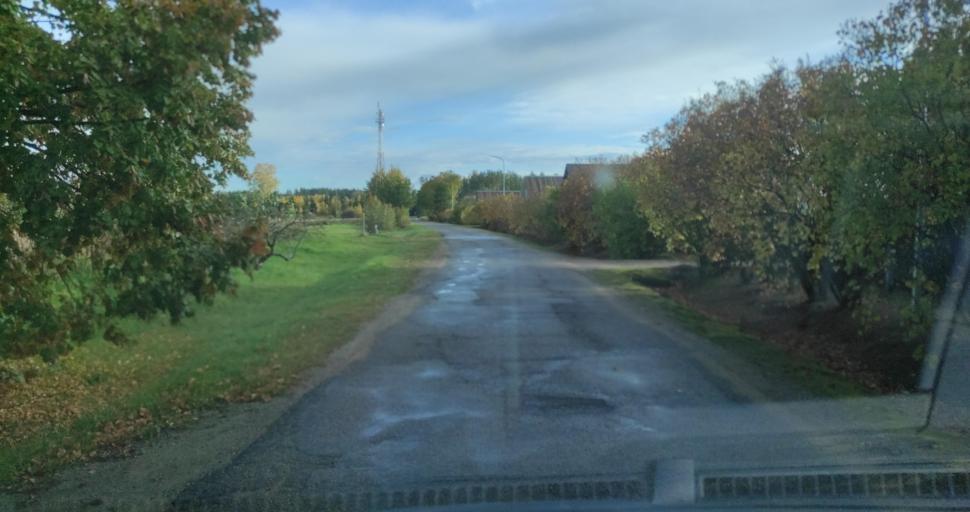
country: LV
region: Skrunda
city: Skrunda
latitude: 56.6831
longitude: 22.0537
